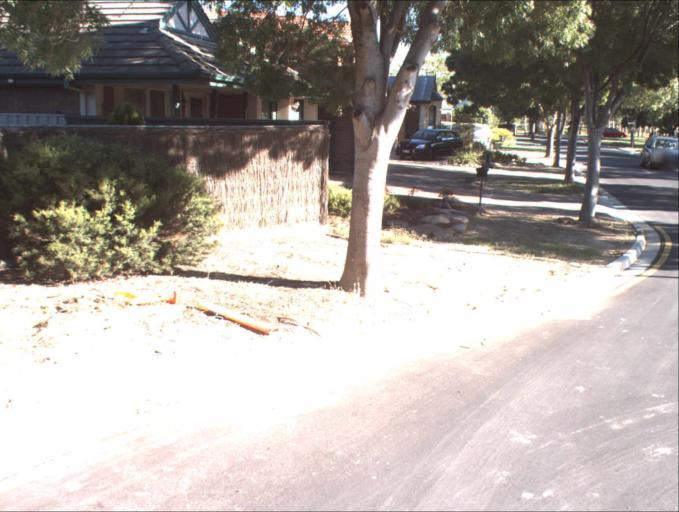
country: AU
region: South Australia
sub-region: Port Adelaide Enfield
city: Gilles Plains
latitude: -34.8578
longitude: 138.6473
